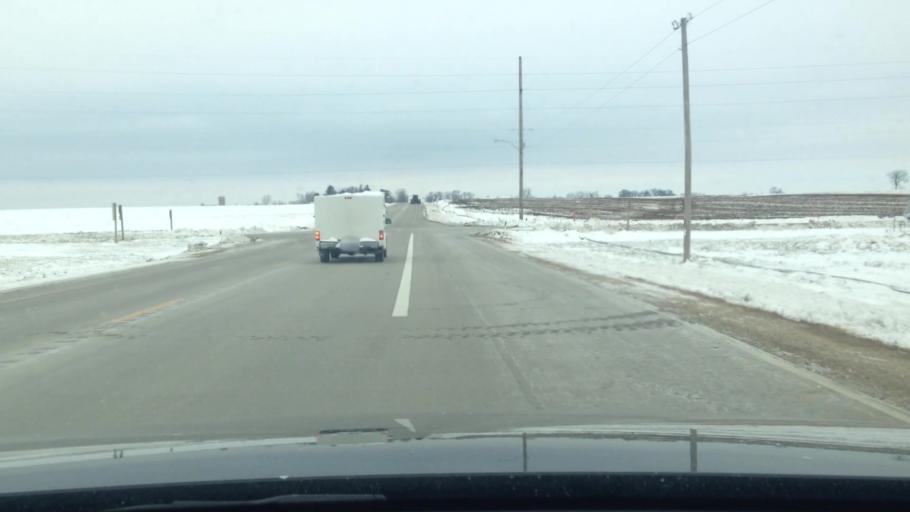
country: US
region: Illinois
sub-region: McHenry County
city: Hebron
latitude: 42.5157
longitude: -88.4427
